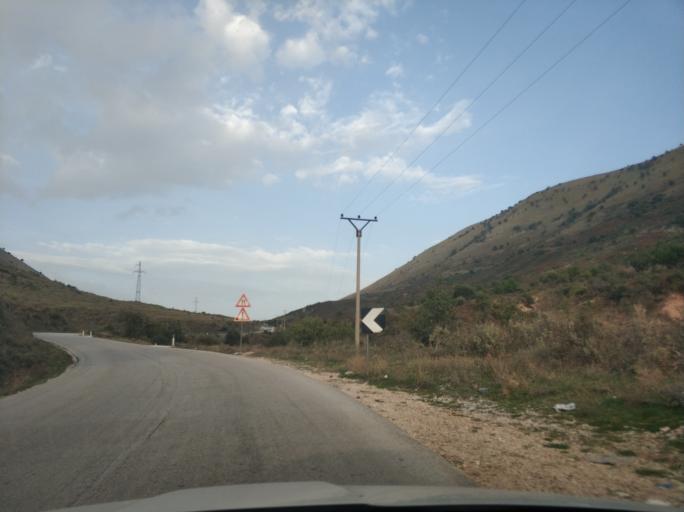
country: AL
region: Gjirokaster
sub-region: Rrethi i Gjirokastres
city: Dervician
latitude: 39.9369
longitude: 20.2155
